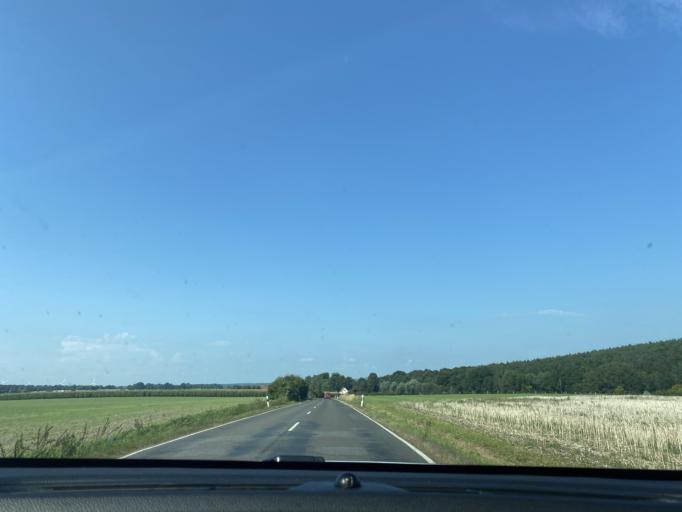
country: DE
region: Saxony
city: Reichenbach
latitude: 51.1646
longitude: 14.7873
